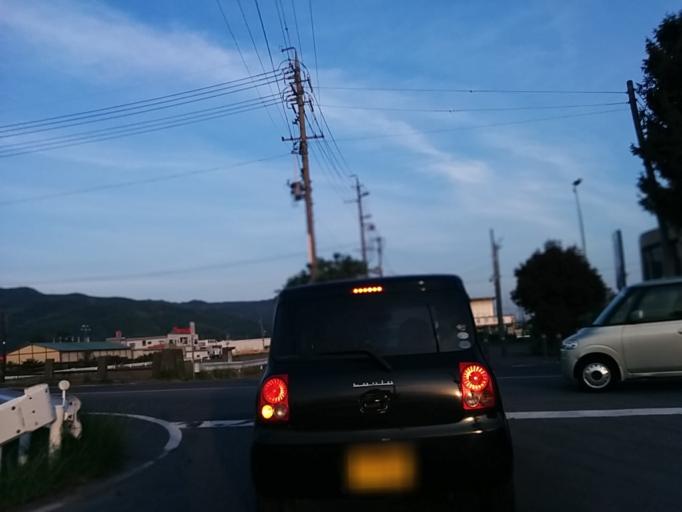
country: JP
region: Nagano
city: Suwa
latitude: 36.0392
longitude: 138.1020
